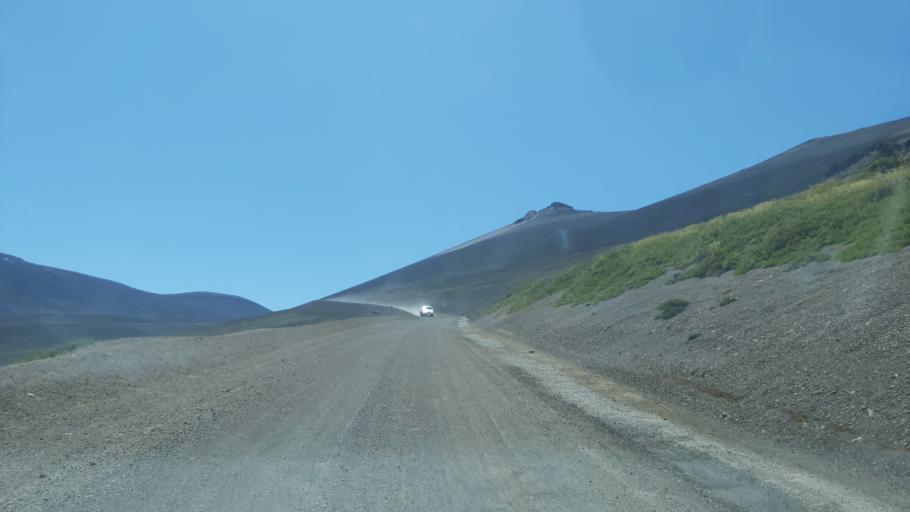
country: CL
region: Araucania
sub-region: Provincia de Cautin
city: Vilcun
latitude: -38.4129
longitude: -71.5419
